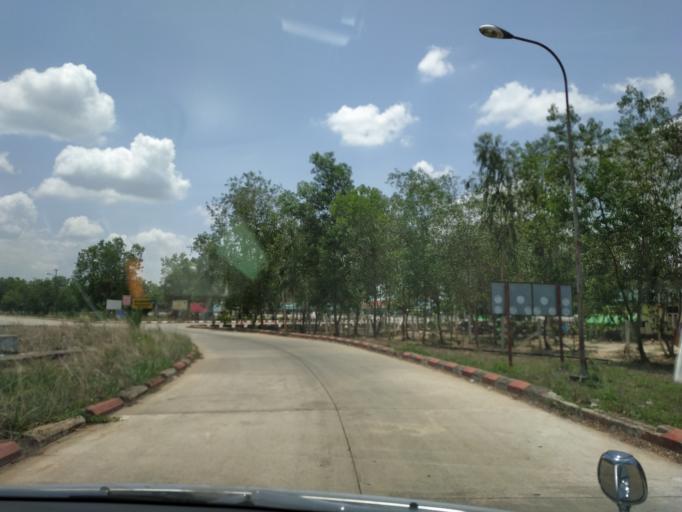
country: MM
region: Bago
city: Bago
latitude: 17.4661
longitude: 96.4512
